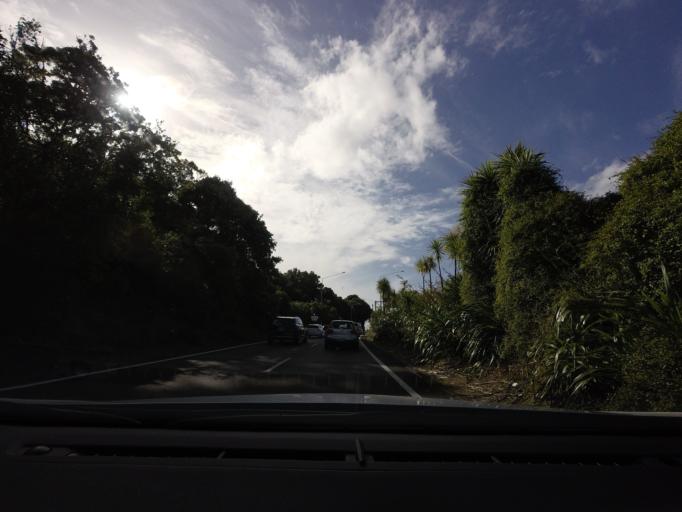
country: NZ
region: Auckland
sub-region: Auckland
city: Auckland
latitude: -36.8721
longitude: 174.7733
